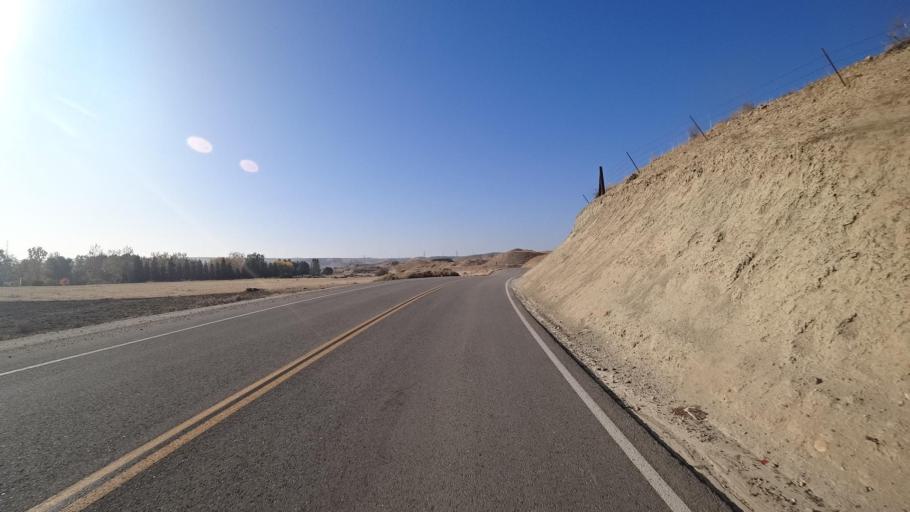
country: US
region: California
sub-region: Kern County
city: Oildale
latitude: 35.4512
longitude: -118.9295
